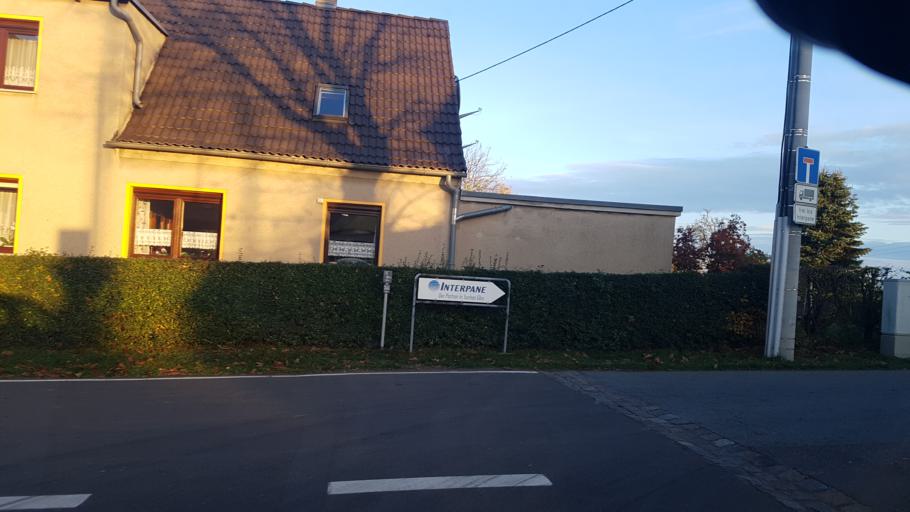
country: DE
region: Saxony
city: Belgern
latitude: 51.4638
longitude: 13.1650
